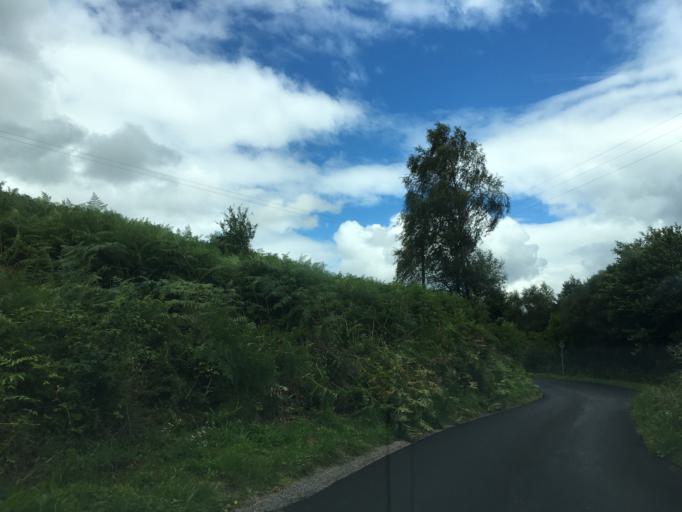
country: GB
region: Scotland
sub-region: Argyll and Bute
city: Oban
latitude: 56.3414
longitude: -5.2008
